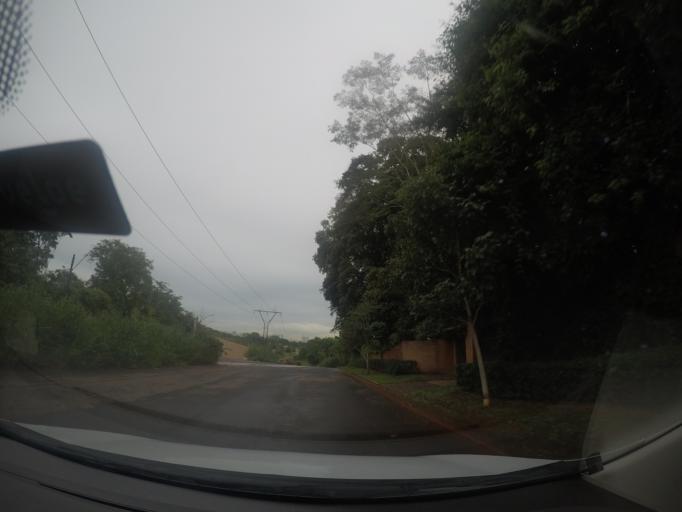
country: BR
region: Goias
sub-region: Goiania
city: Goiania
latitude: -16.6319
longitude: -49.2401
